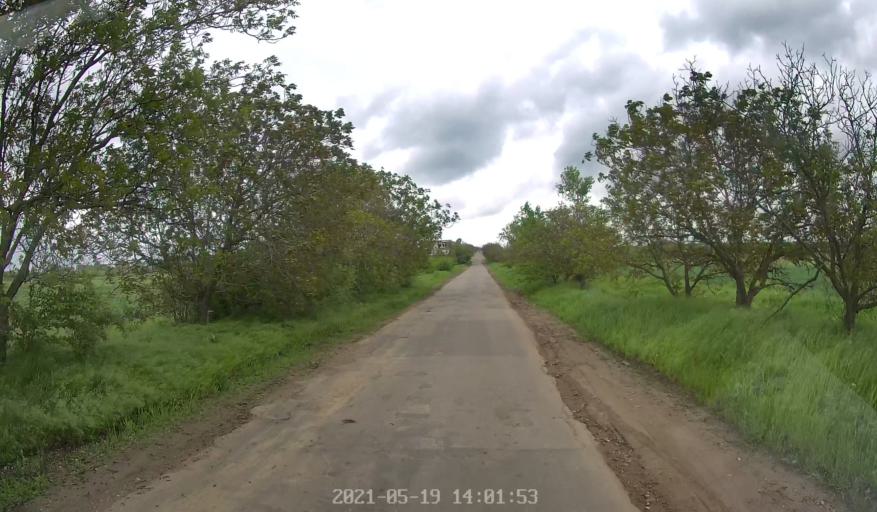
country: MD
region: Chisinau
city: Chisinau
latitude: 47.0332
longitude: 28.9405
